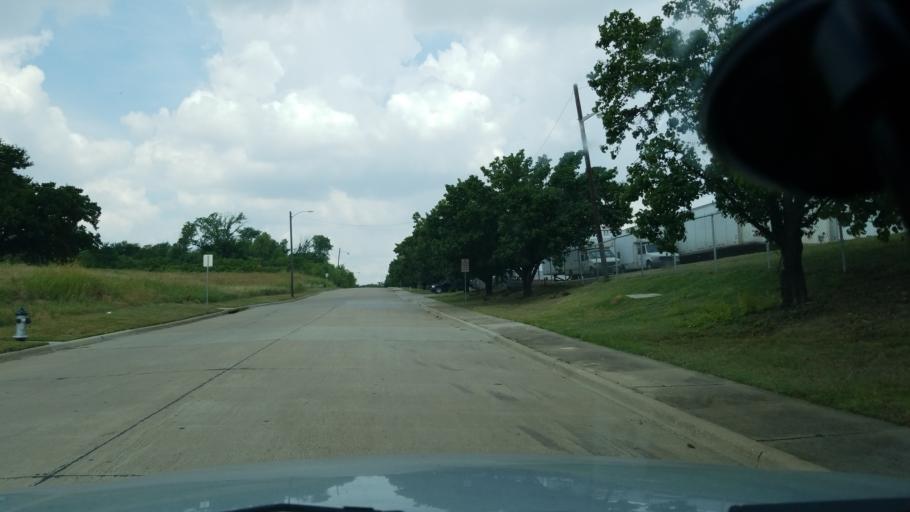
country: US
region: Texas
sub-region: Dallas County
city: Irving
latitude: 32.8326
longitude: -96.8984
